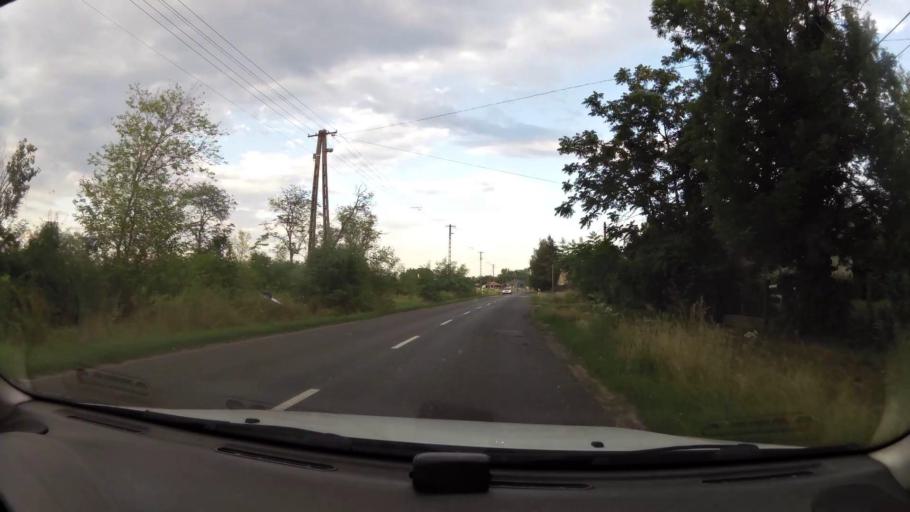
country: HU
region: Pest
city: Tapiobicske
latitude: 47.3557
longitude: 19.6977
